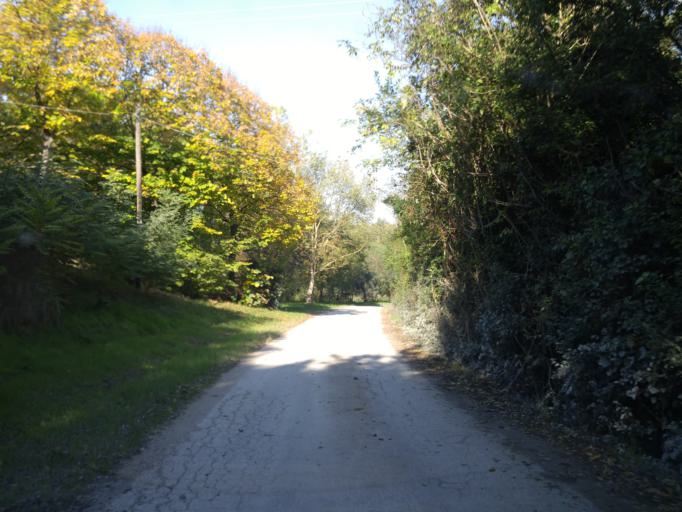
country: IT
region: The Marches
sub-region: Provincia di Pesaro e Urbino
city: Calcinelli
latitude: 43.7426
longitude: 12.9228
